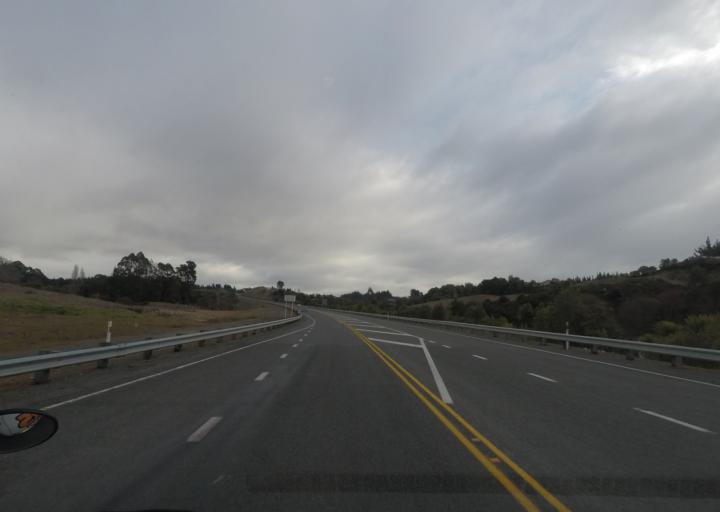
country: NZ
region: Tasman
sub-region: Tasman District
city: Mapua
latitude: -41.2507
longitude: 173.0682
